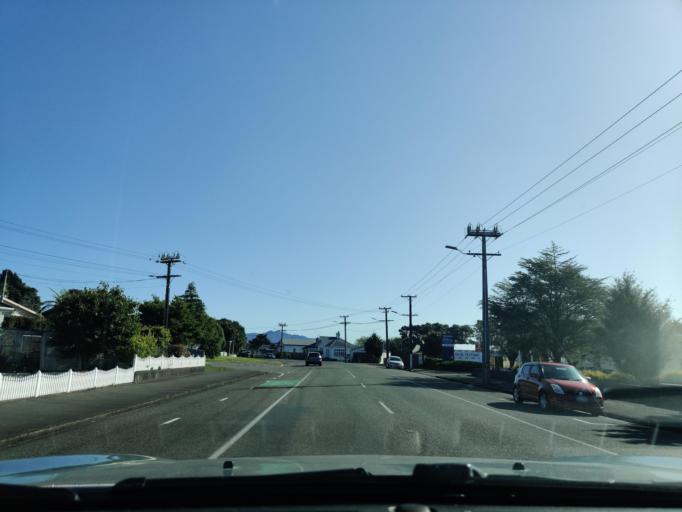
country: NZ
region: Taranaki
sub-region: New Plymouth District
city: New Plymouth
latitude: -39.0745
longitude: 174.0580
